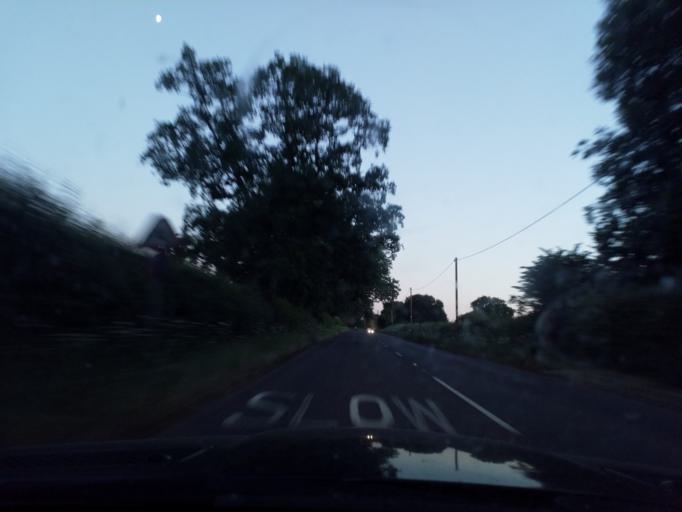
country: GB
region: England
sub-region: Solihull
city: Balsall Common
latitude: 52.3693
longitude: -1.6385
